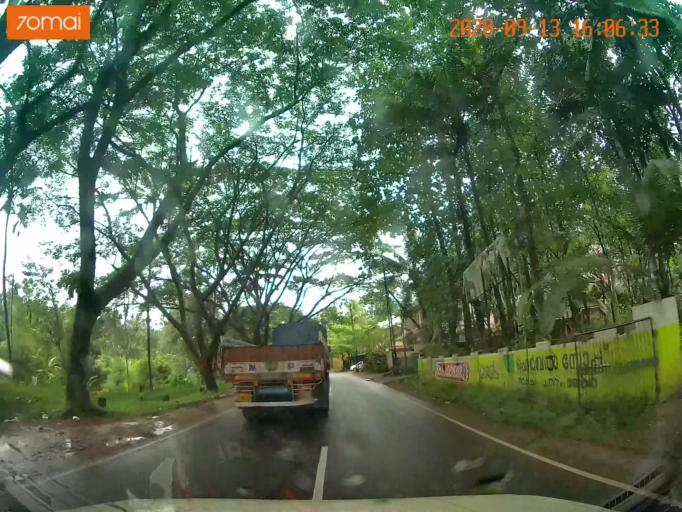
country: IN
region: Kerala
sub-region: Kottayam
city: Palackattumala
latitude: 9.6715
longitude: 76.5819
